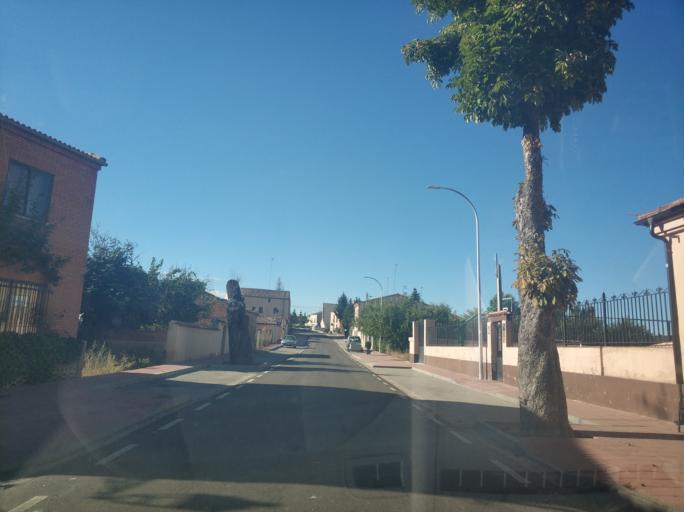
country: ES
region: Castille and Leon
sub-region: Provincia de Burgos
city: San Juan del Monte
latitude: 41.6844
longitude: -3.5222
